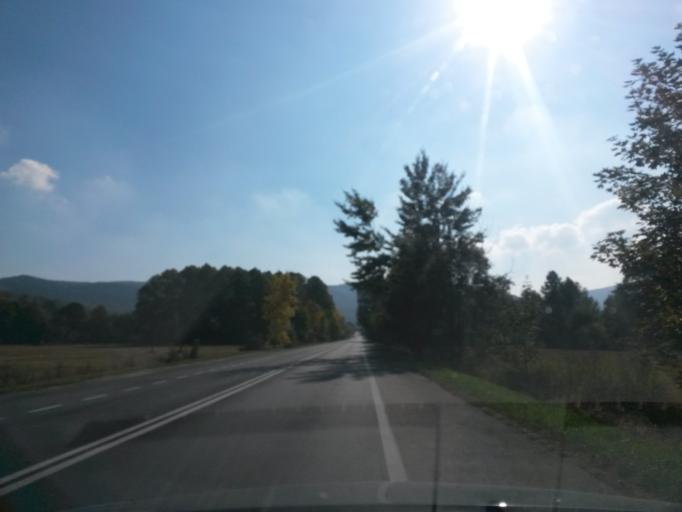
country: PL
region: Lower Silesian Voivodeship
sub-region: Powiat jeleniogorski
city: Kowary
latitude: 50.7996
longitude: 15.8412
